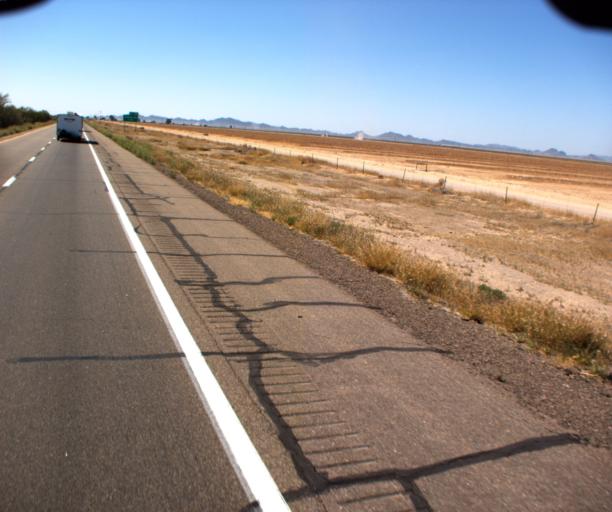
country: US
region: Arizona
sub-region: Maricopa County
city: Gila Bend
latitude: 32.9251
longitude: -112.8648
